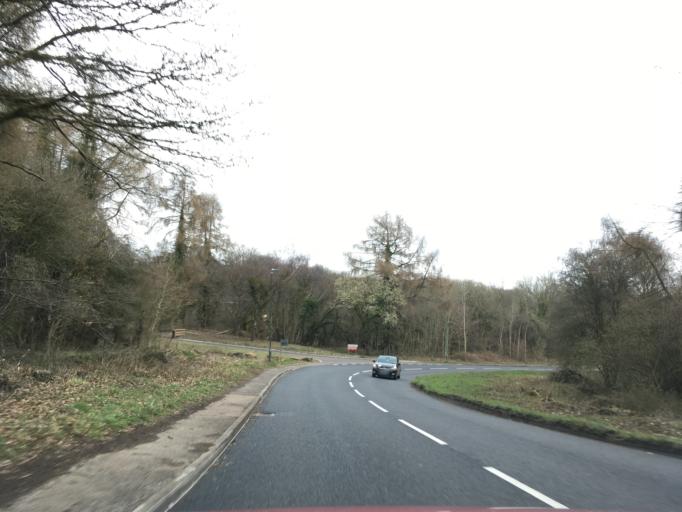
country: GB
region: England
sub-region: Gloucestershire
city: Coleford
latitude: 51.8065
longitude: -2.6068
